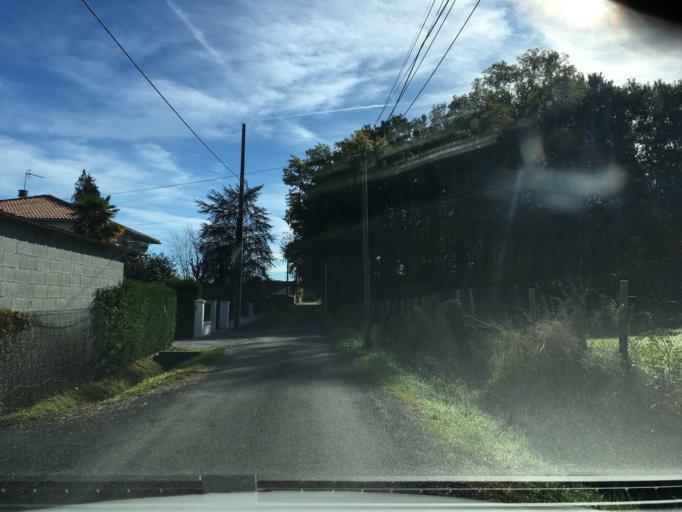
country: FR
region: Aquitaine
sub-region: Departement des Pyrenees-Atlantiques
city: Idron
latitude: 43.3131
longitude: -0.3186
